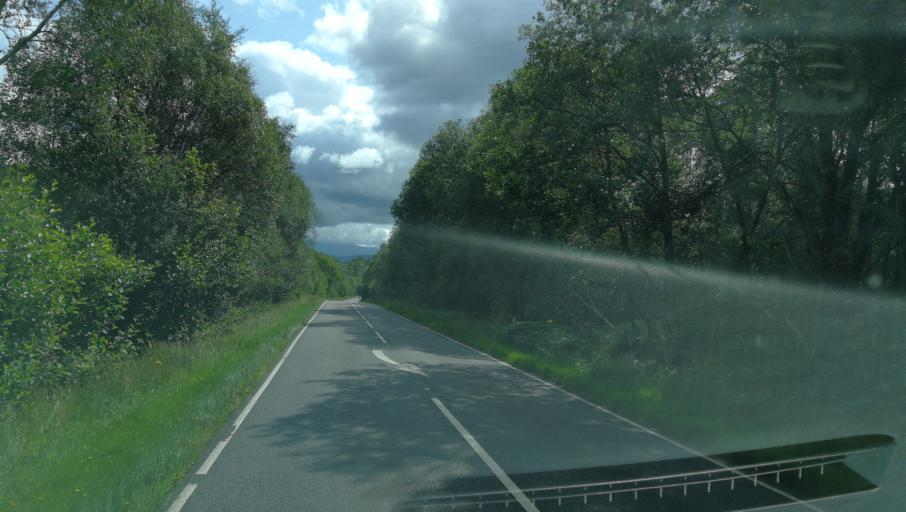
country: GB
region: Scotland
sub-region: Highland
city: Fort William
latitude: 56.8621
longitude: -5.3782
